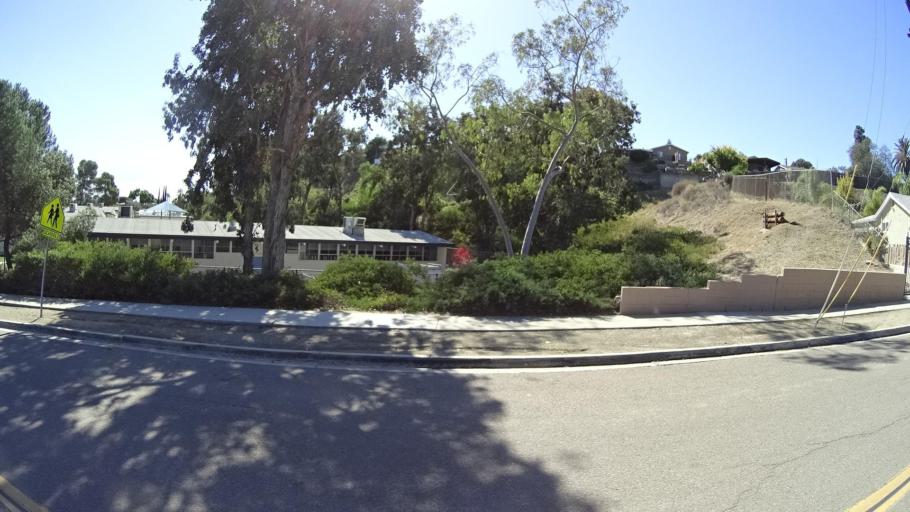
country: US
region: California
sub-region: San Diego County
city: La Presa
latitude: 32.7193
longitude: -117.0181
